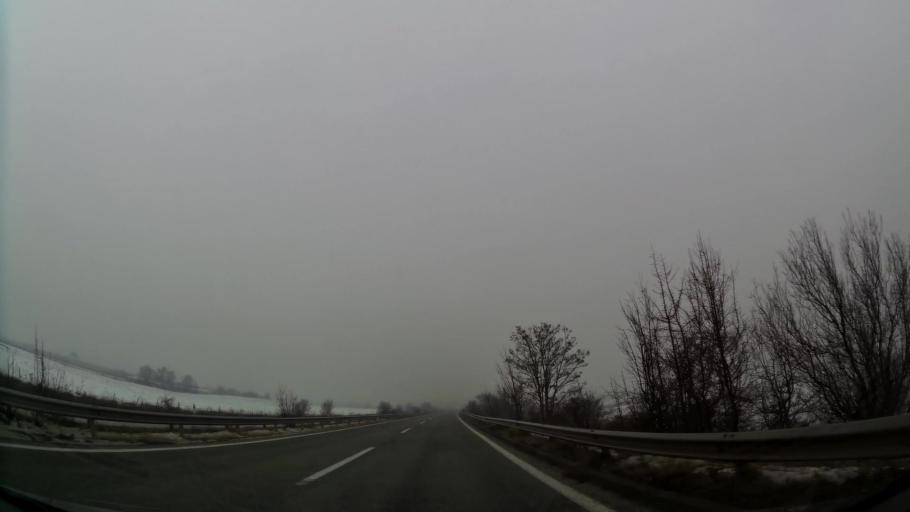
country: MK
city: Miladinovci
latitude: 41.9704
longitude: 21.6458
